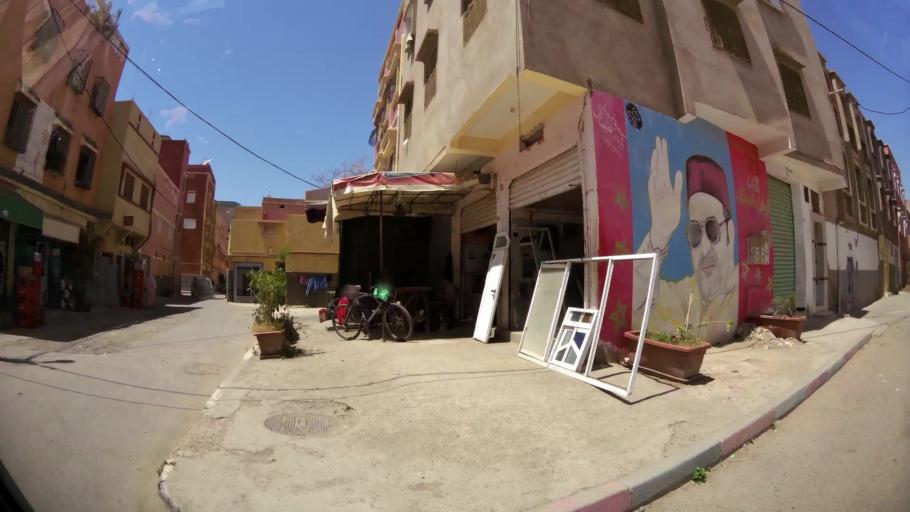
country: MA
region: Souss-Massa-Draa
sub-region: Inezgane-Ait Mellou
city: Inezgane
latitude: 30.3440
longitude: -9.4975
